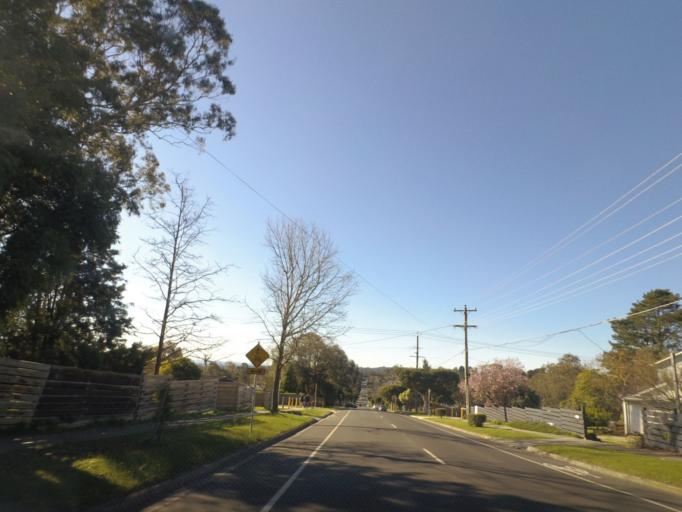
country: AU
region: Victoria
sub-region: Yarra Ranges
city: Kilsyth
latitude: -37.7981
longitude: 145.3131
